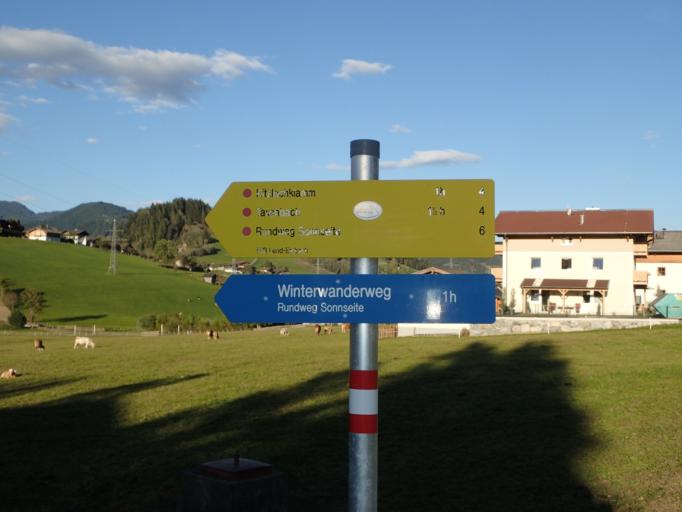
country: AT
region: Salzburg
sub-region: Politischer Bezirk Zell am See
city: Taxenbach
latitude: 47.2896
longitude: 12.9968
